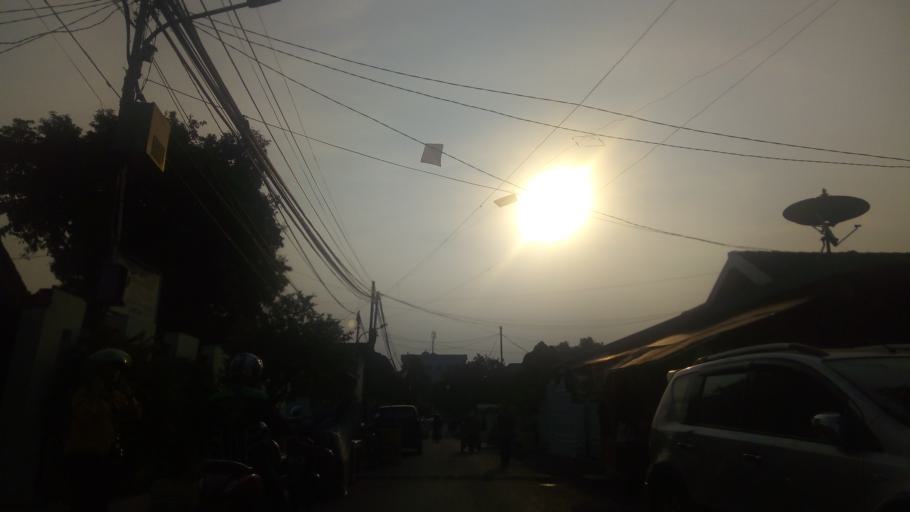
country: ID
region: Jakarta Raya
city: Jakarta
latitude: -6.2035
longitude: 106.8533
